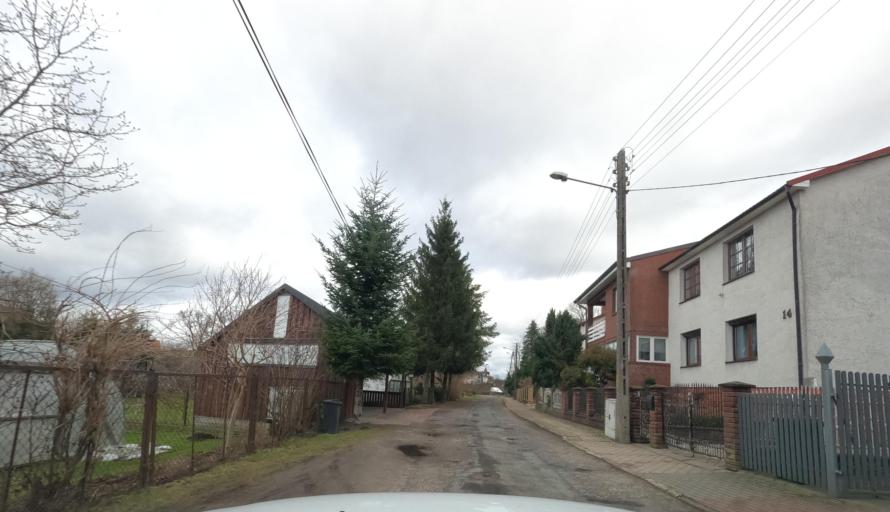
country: PL
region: West Pomeranian Voivodeship
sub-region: Powiat choszczenski
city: Recz
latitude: 53.2569
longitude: 15.5462
